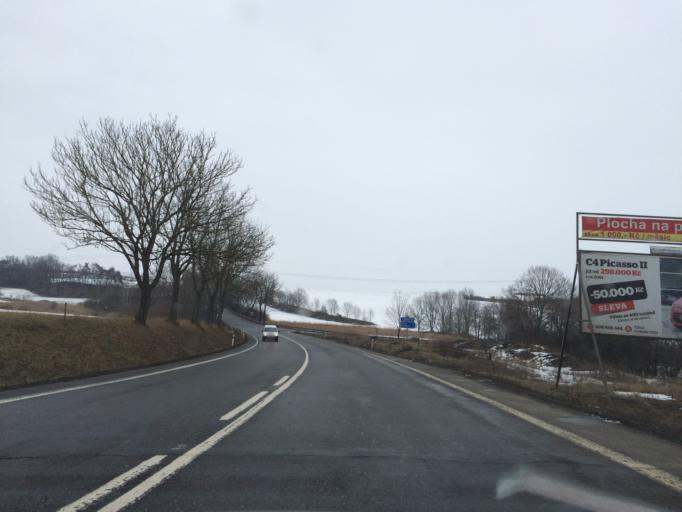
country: CZ
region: Jihocesky
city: Radomysl
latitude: 49.2773
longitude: 13.9453
